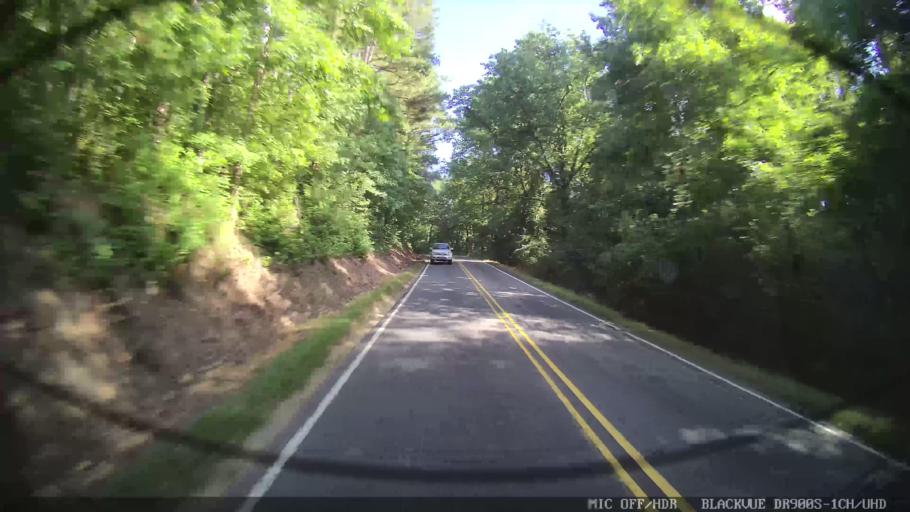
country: US
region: Georgia
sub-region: Floyd County
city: Lindale
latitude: 34.1877
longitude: -85.0572
